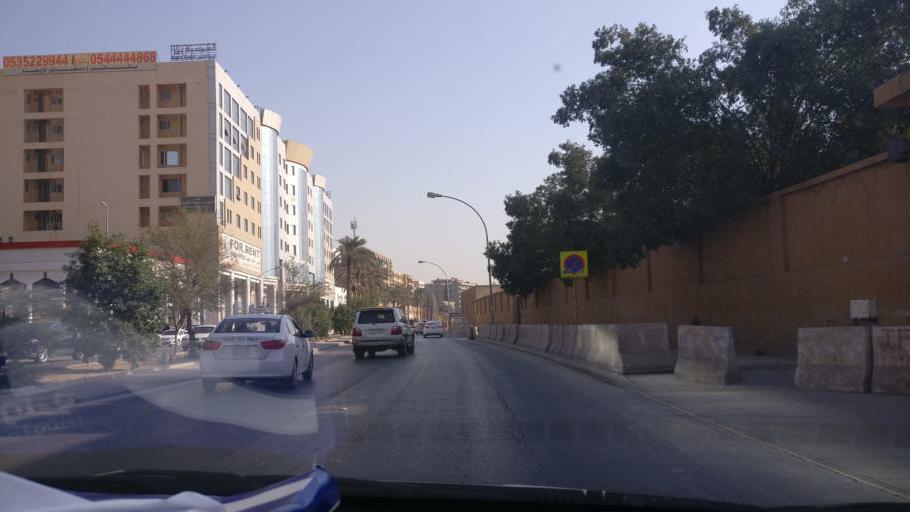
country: SA
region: Ar Riyad
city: Riyadh
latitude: 24.6437
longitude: 46.7136
